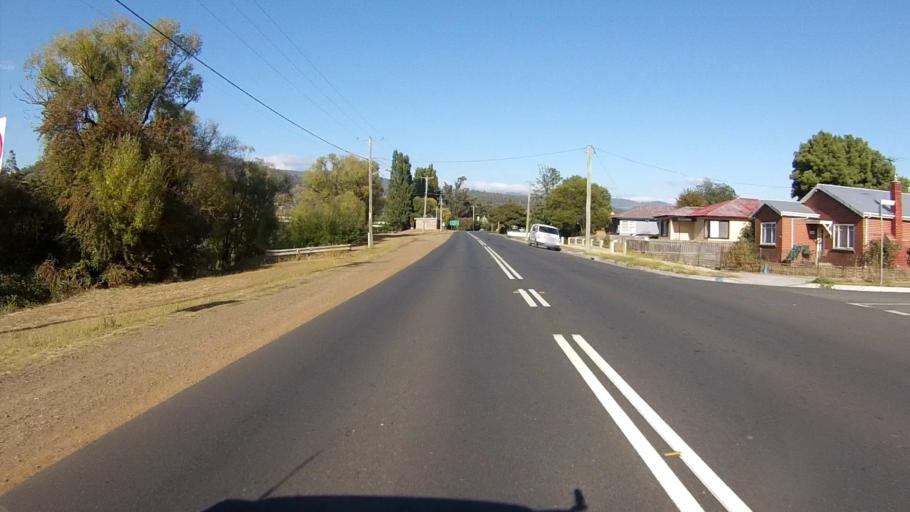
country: AU
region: Tasmania
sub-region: Derwent Valley
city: New Norfolk
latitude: -42.7766
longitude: 147.0594
